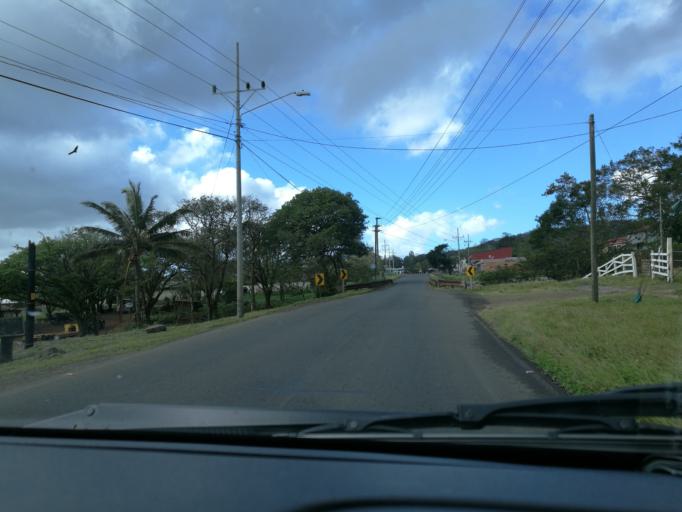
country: CR
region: Alajuela
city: Bijagua
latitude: 10.6836
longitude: -85.0878
